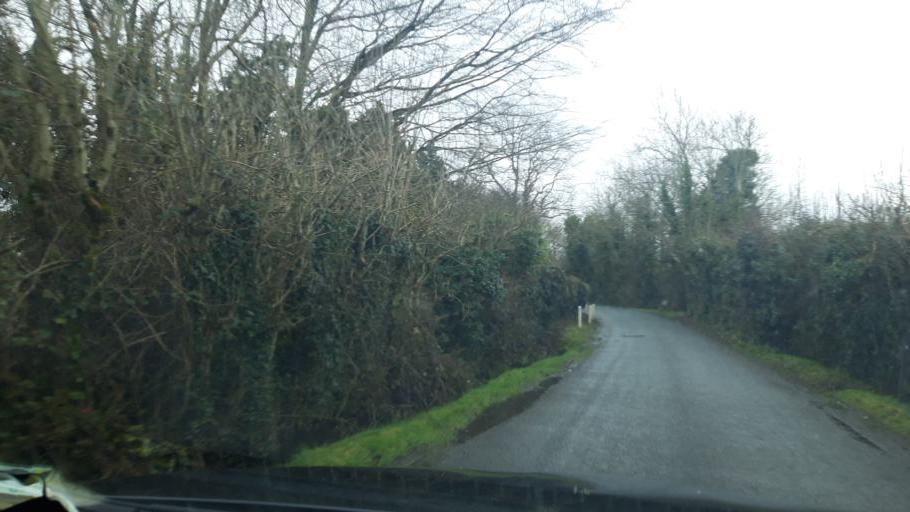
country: IE
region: Leinster
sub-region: South Dublin
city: Newcastle
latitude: 53.3309
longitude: -6.5032
